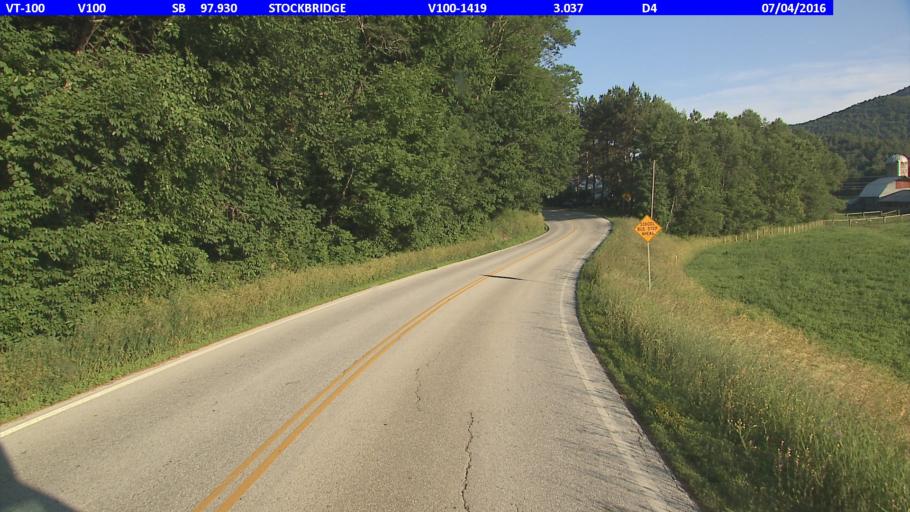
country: US
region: Vermont
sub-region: Orange County
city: Randolph
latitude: 43.7850
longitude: -72.7552
